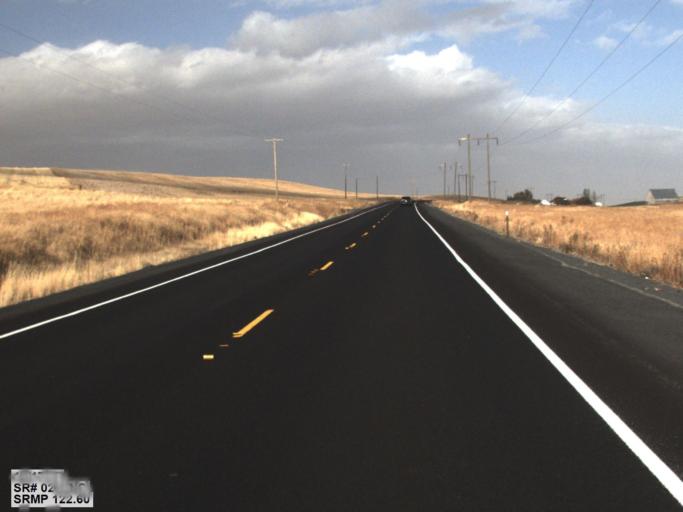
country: US
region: Washington
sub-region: Lincoln County
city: Davenport
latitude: 47.5370
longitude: -118.1971
